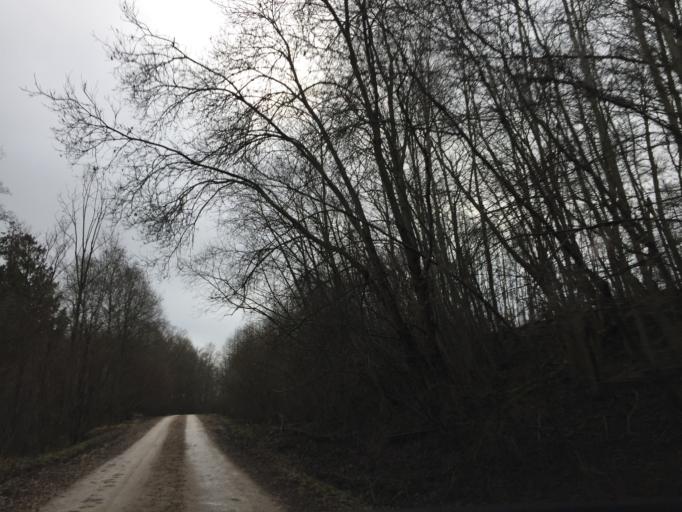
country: LV
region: Broceni
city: Broceni
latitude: 56.6806
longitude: 22.5580
